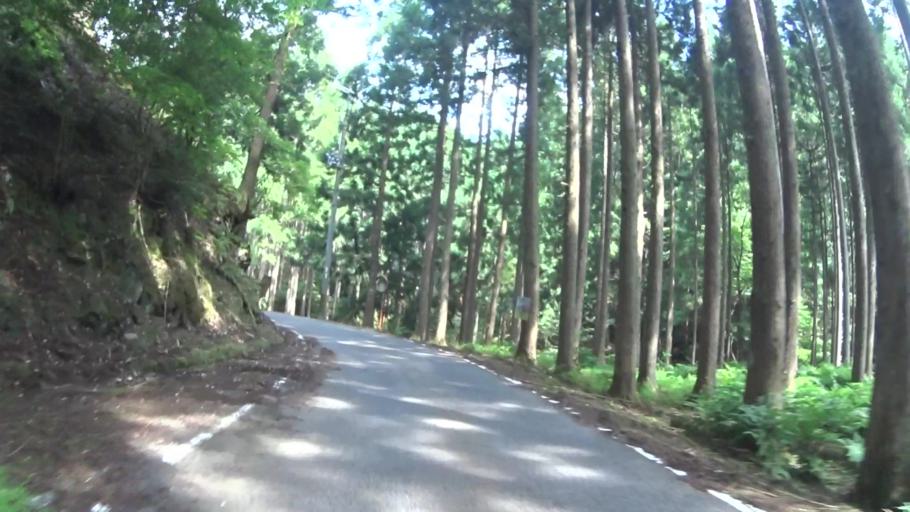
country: JP
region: Fukui
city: Obama
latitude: 35.2946
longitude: 135.6363
